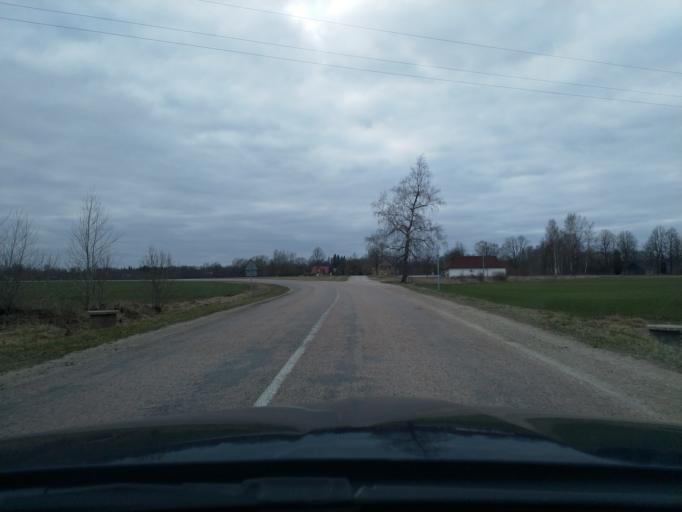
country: LV
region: Talsu Rajons
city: Sabile
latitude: 56.9600
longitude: 22.6215
